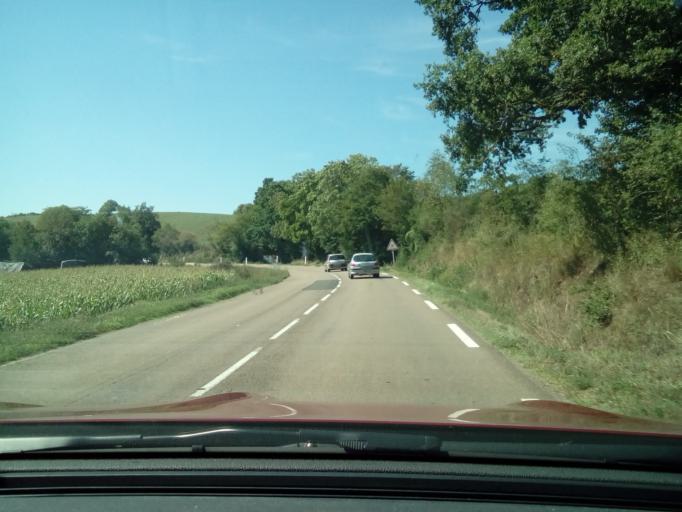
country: FR
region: Rhone-Alpes
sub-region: Departement du Rhone
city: Saint-Verand
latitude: 45.9029
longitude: 4.5471
